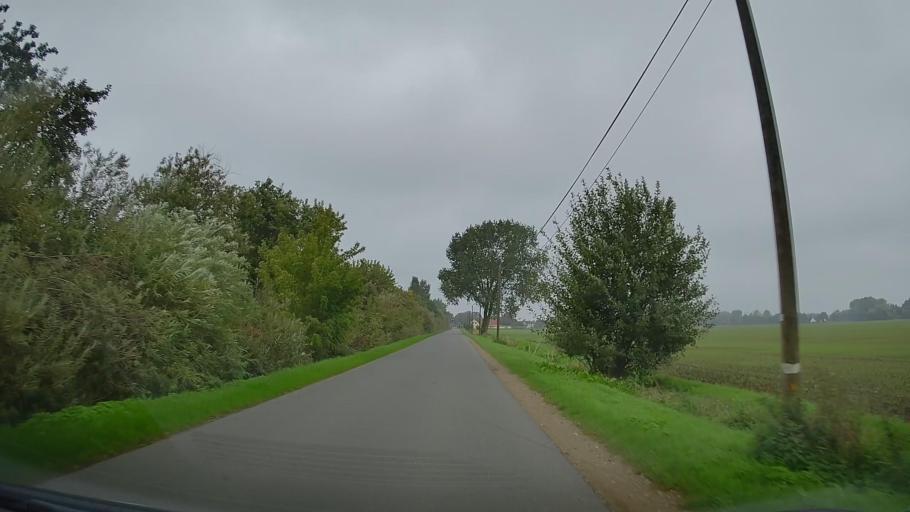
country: DE
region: Mecklenburg-Vorpommern
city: Neubukow
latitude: 54.0515
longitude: 11.6170
